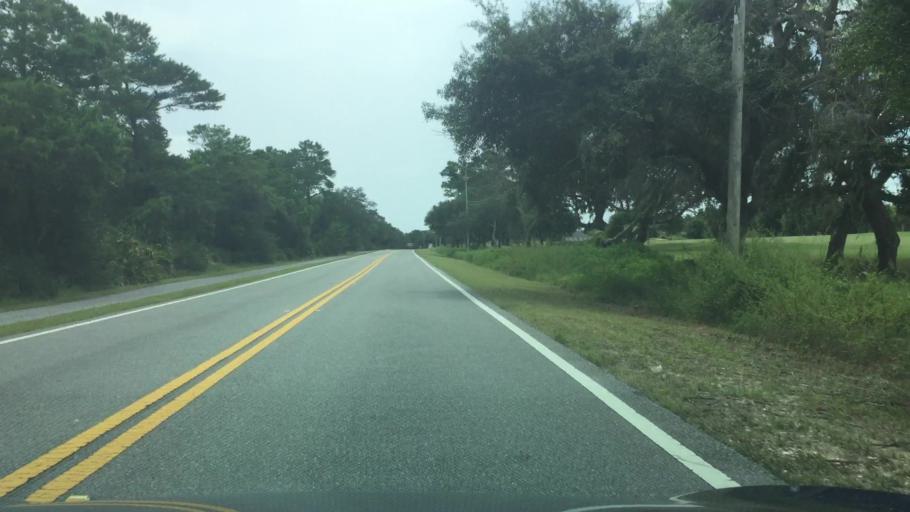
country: US
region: Florida
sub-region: Bay County
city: Upper Grand Lagoon
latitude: 30.1480
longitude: -85.7183
